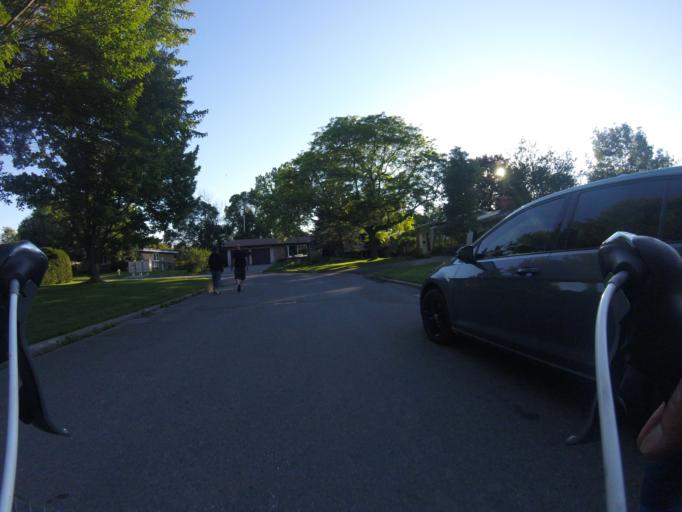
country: CA
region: Ontario
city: Bells Corners
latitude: 45.3492
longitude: -75.8384
